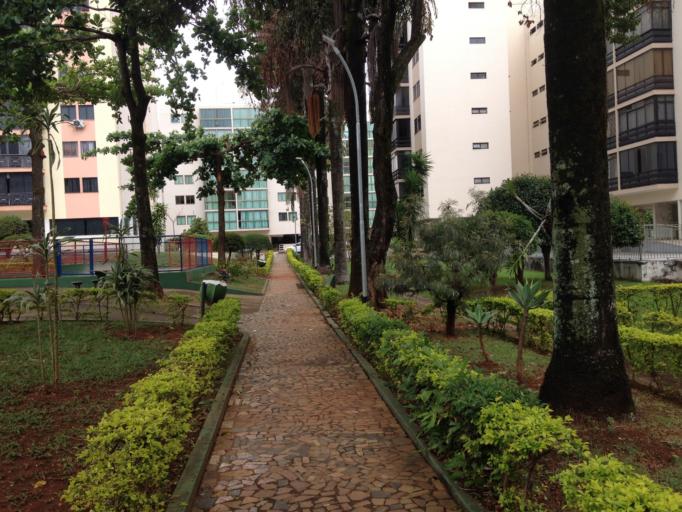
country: BR
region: Federal District
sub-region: Brasilia
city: Brasilia
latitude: -15.8078
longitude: -47.9387
